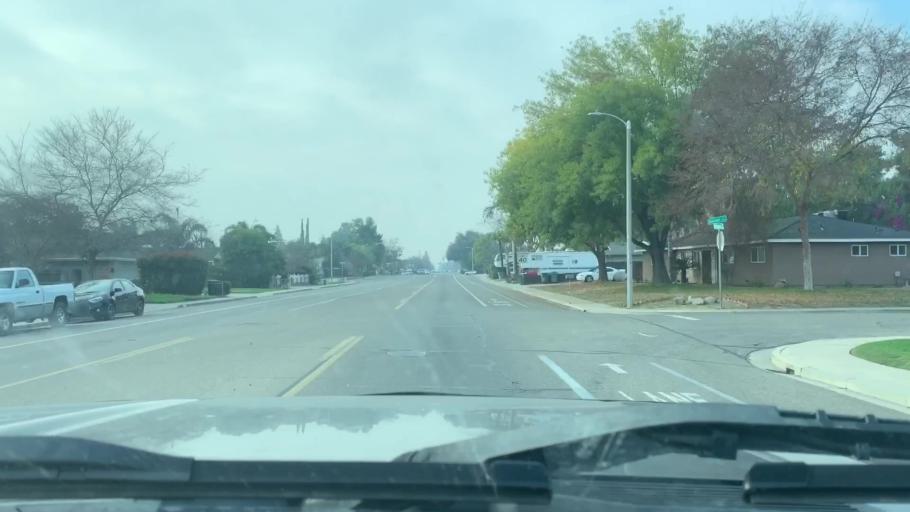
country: US
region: California
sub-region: Tulare County
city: Visalia
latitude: 36.3057
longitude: -119.3068
